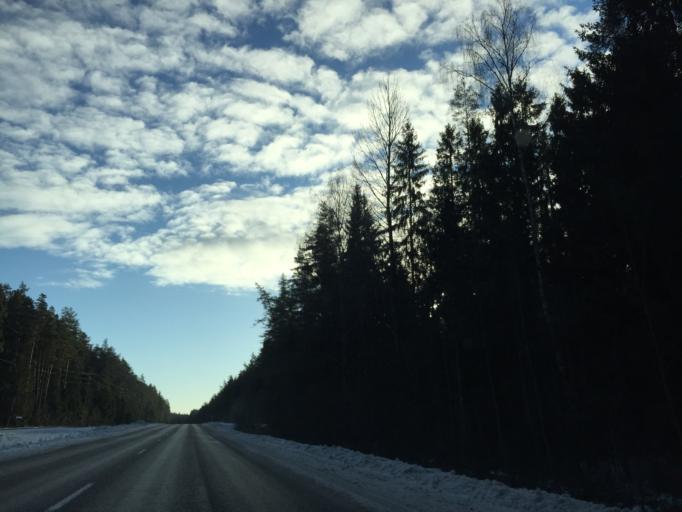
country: LV
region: Kegums
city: Kegums
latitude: 56.7215
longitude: 24.7133
